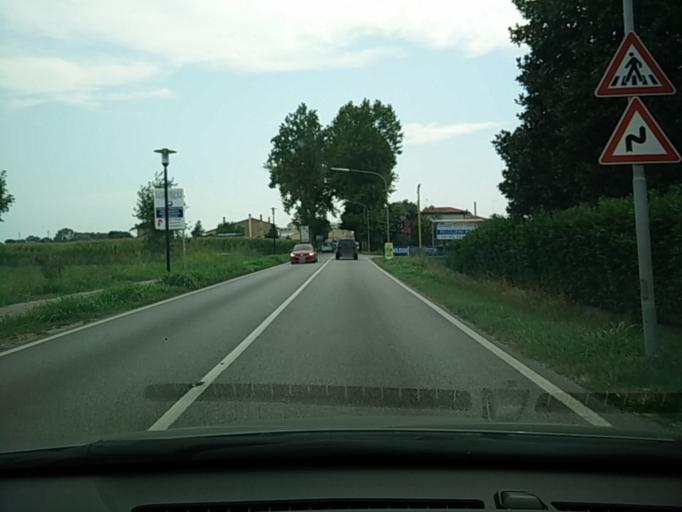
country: IT
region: Veneto
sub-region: Provincia di Venezia
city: Iesolo
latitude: 45.5427
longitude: 12.6504
